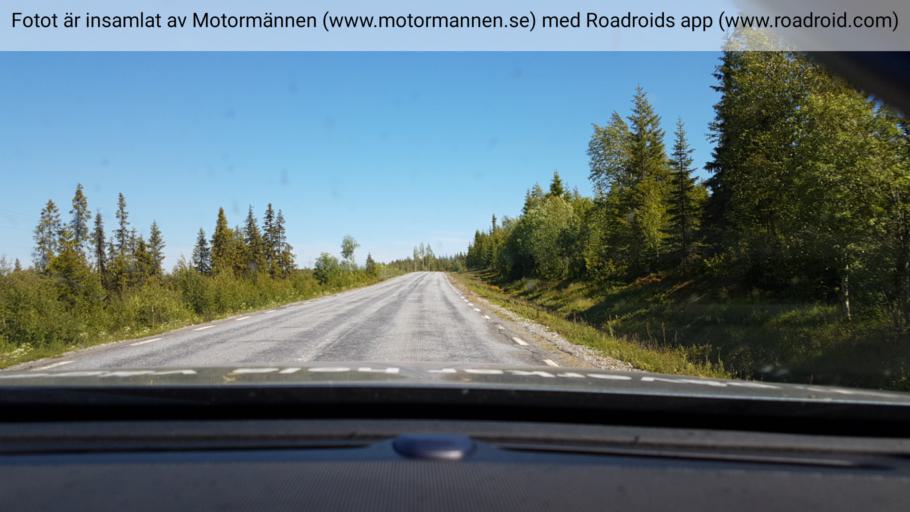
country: SE
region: Vaesterbotten
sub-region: Vilhelmina Kommun
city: Sjoberg
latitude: 64.7448
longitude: 16.1872
